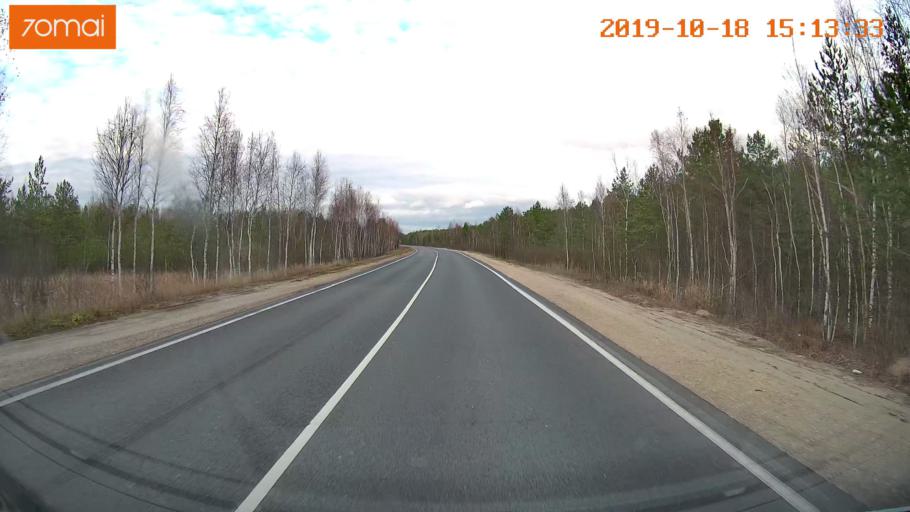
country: RU
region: Vladimir
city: Gus'-Khrustal'nyy
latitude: 55.5886
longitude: 40.7177
